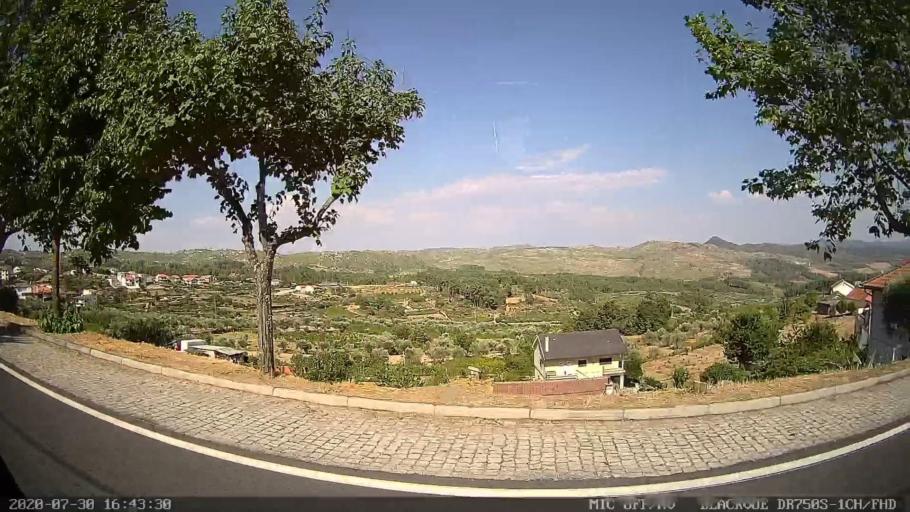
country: PT
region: Vila Real
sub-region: Sabrosa
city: Sabrosa
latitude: 41.2875
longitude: -7.4776
